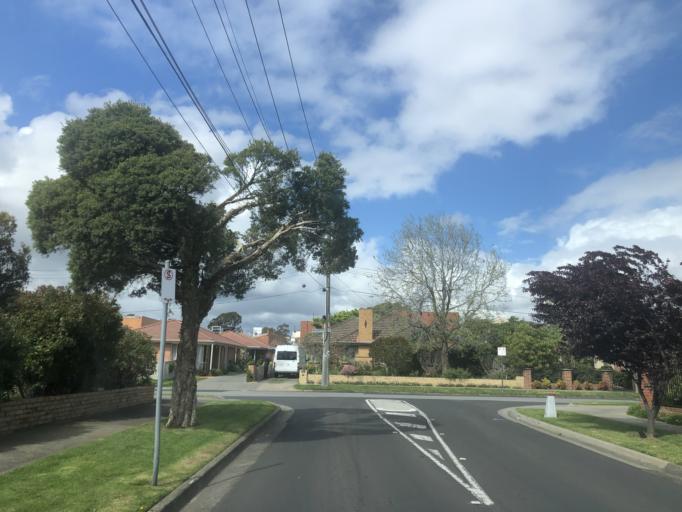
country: AU
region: Victoria
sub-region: Monash
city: Ashwood
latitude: -37.8762
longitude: 145.1261
